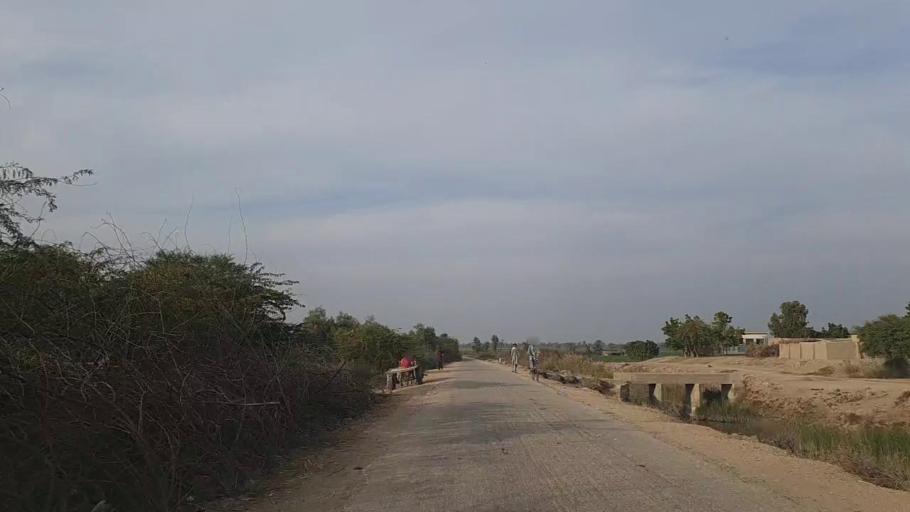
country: PK
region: Sindh
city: Daur
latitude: 26.4830
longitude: 68.4641
